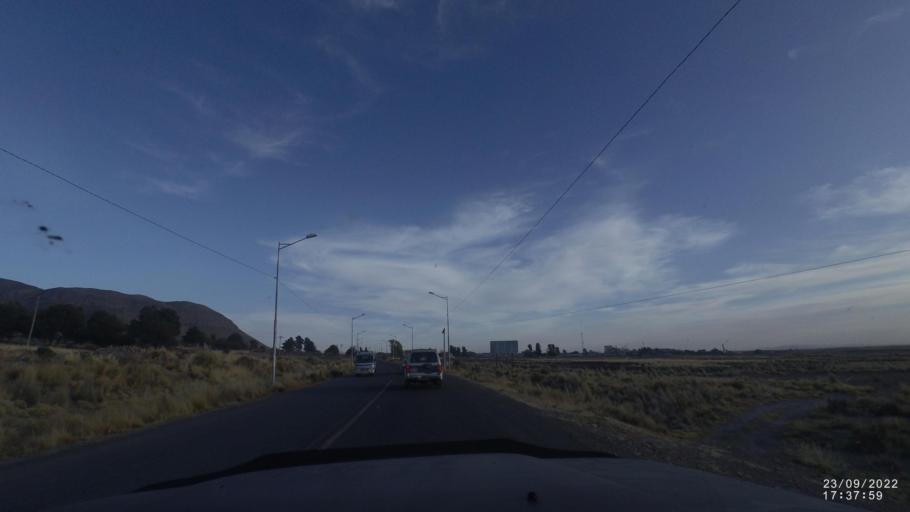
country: BO
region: Oruro
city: Challapata
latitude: -19.0014
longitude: -66.7772
